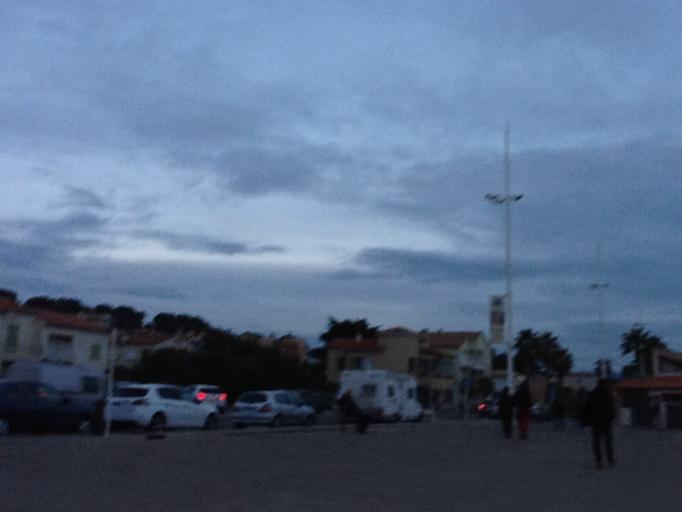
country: FR
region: Provence-Alpes-Cote d'Azur
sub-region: Departement du Var
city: Sanary-sur-Mer
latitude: 43.1123
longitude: 5.8114
